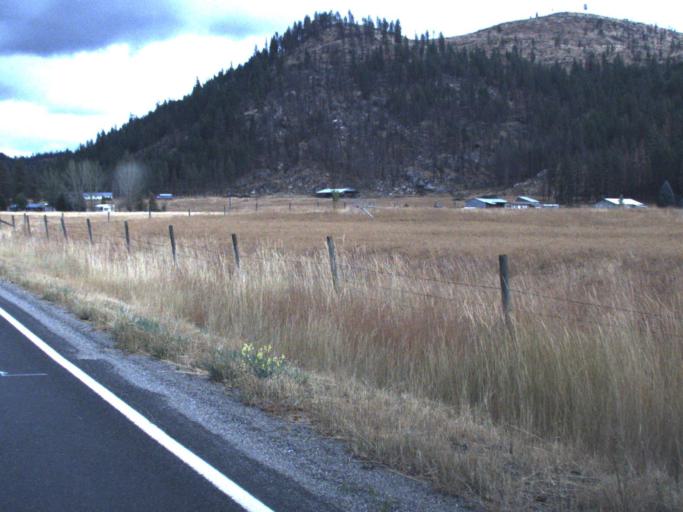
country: US
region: Washington
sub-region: Spokane County
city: Deer Park
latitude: 47.9632
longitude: -117.7453
